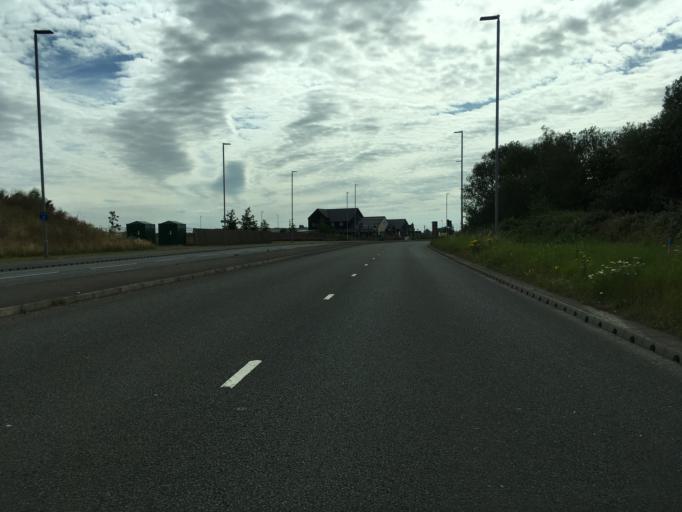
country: GB
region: Wales
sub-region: Newport
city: Llanwern
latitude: 51.5736
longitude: -2.9338
